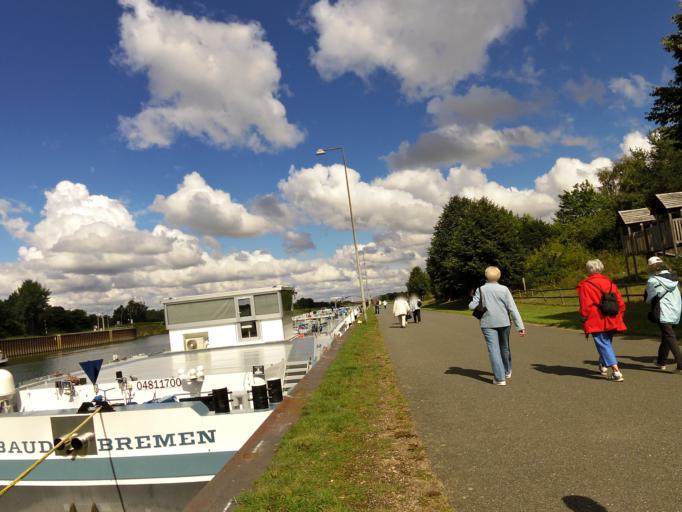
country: DE
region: Lower Saxony
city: Scharnebeck
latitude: 53.2965
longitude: 10.4897
